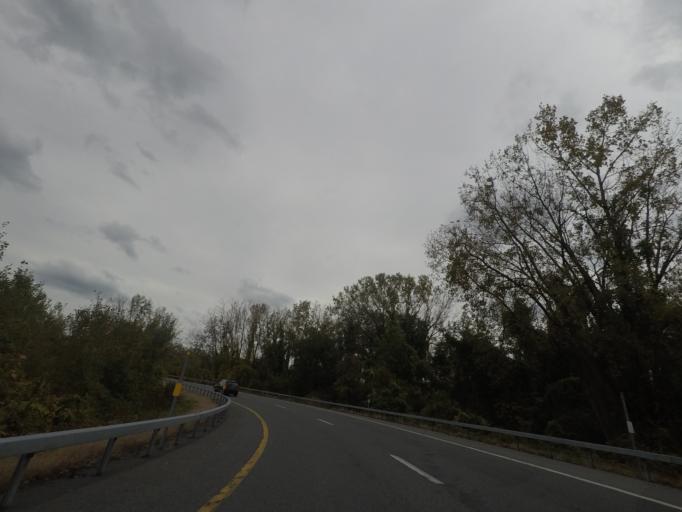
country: US
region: New York
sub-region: Albany County
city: Roessleville
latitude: 42.6882
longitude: -73.8035
